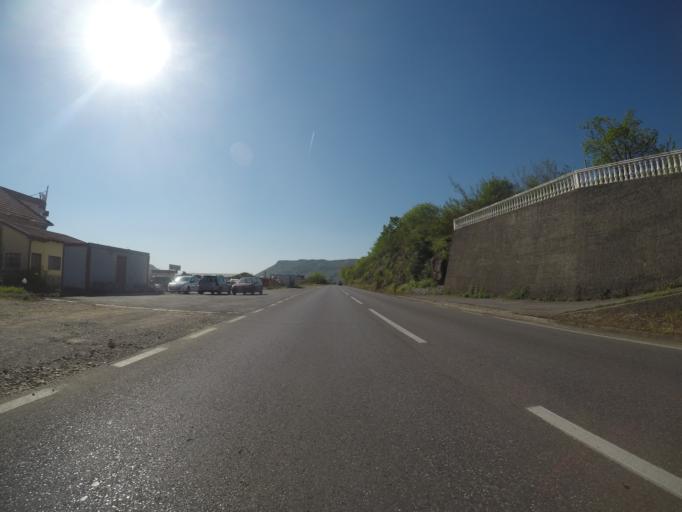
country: ME
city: Spuz
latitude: 42.4762
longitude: 19.1711
